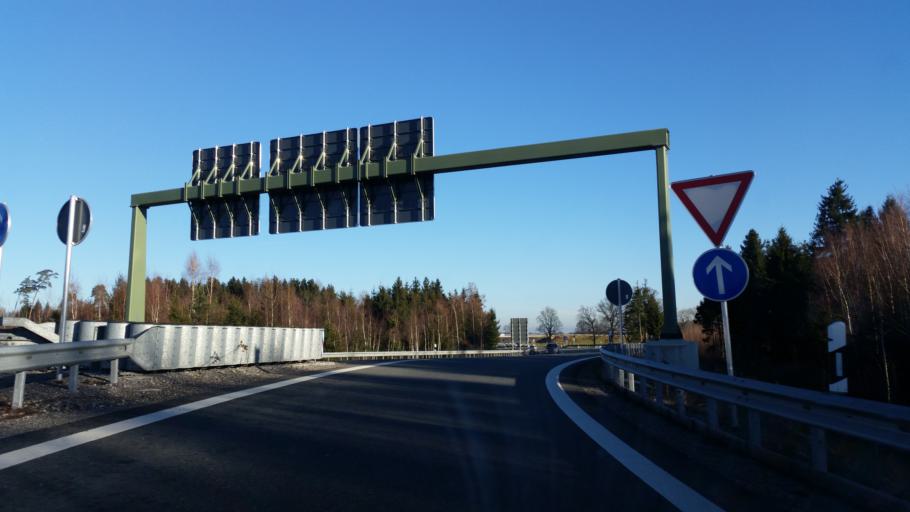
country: DE
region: Bavaria
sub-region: Upper Bavaria
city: Kolbermoor
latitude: 47.8153
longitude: 12.0668
